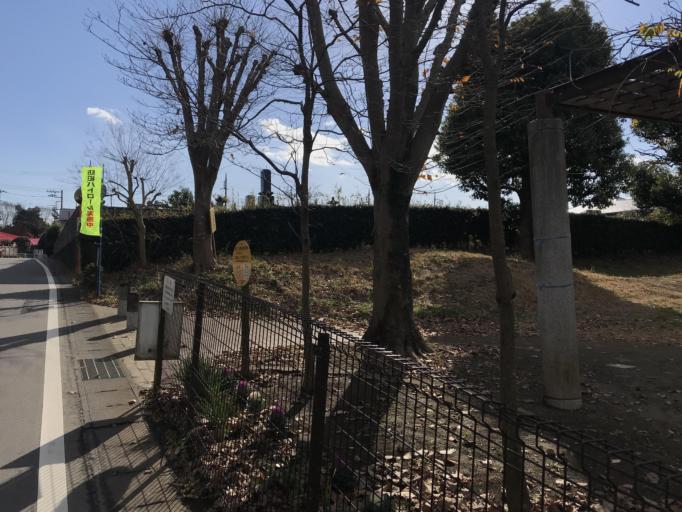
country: JP
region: Ibaraki
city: Ushiku
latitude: 35.9713
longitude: 140.1546
